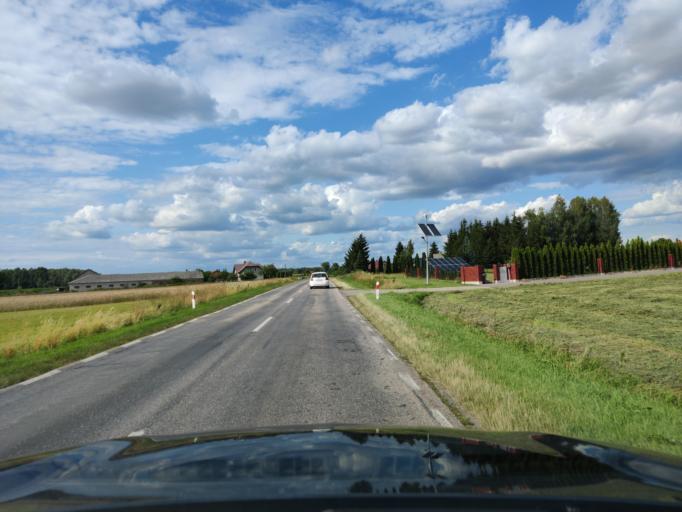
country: PL
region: Podlasie
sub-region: Powiat zambrowski
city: Zambrow
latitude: 52.9069
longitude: 22.2542
